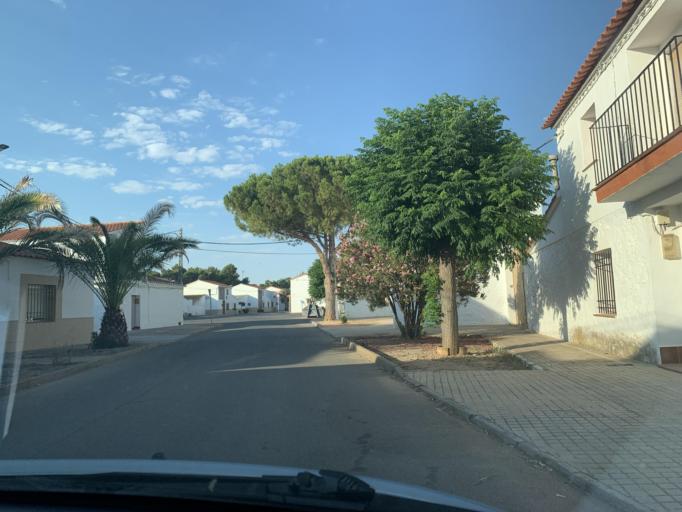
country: ES
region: Castille-La Mancha
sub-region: Provincia de Ciudad Real
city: Argamasilla de Alba
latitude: 39.1760
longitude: -3.2354
